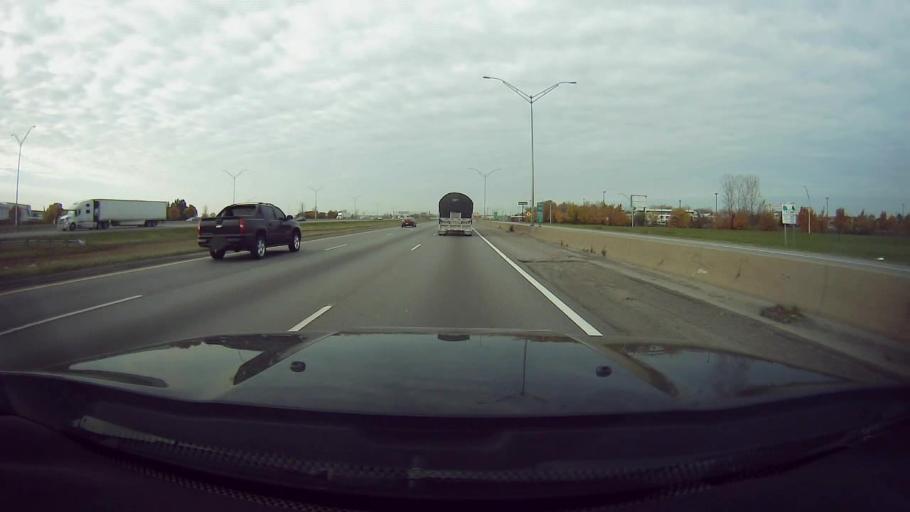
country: US
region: Michigan
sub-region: Wayne County
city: Romulus
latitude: 42.2391
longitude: -83.3426
